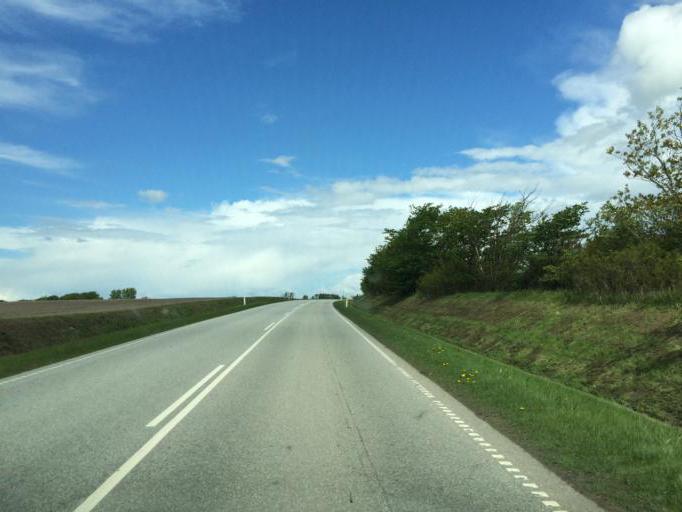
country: DK
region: North Denmark
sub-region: Vesthimmerland Kommune
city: Farso
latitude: 56.8261
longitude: 9.3702
